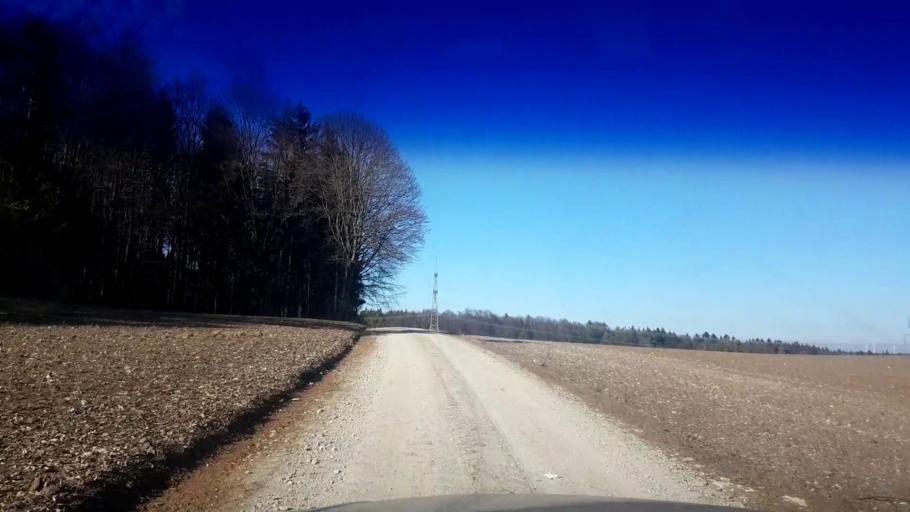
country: DE
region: Bavaria
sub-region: Upper Franconia
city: Poxdorf
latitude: 49.9627
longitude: 11.0863
